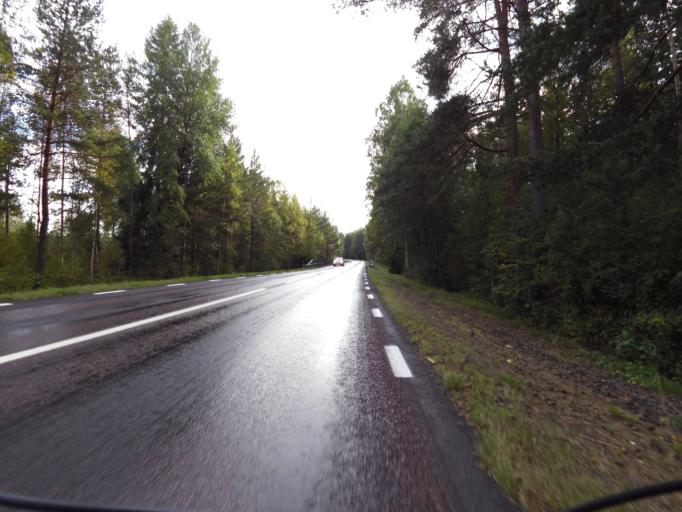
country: SE
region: Gaevleborg
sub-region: Ockelbo Kommun
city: Ockelbo
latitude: 60.8330
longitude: 16.7001
